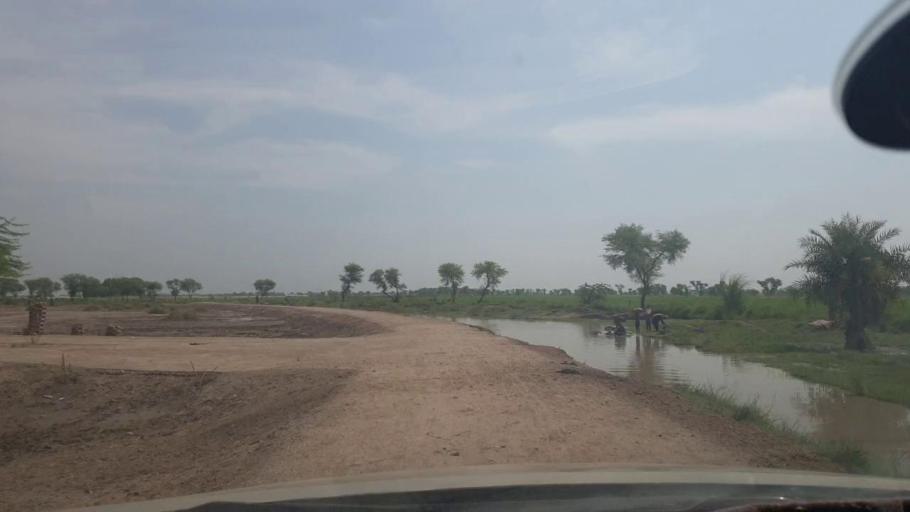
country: PK
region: Sindh
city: Jacobabad
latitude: 28.2729
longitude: 68.5287
